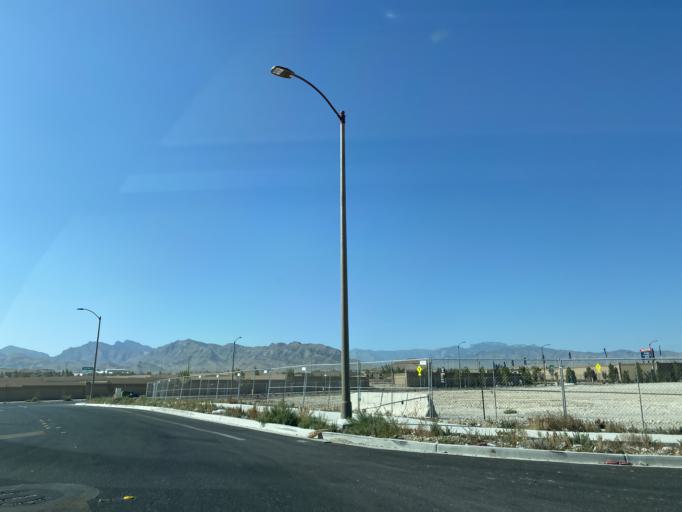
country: US
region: Nevada
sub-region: Clark County
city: Summerlin South
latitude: 36.3169
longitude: -115.3110
